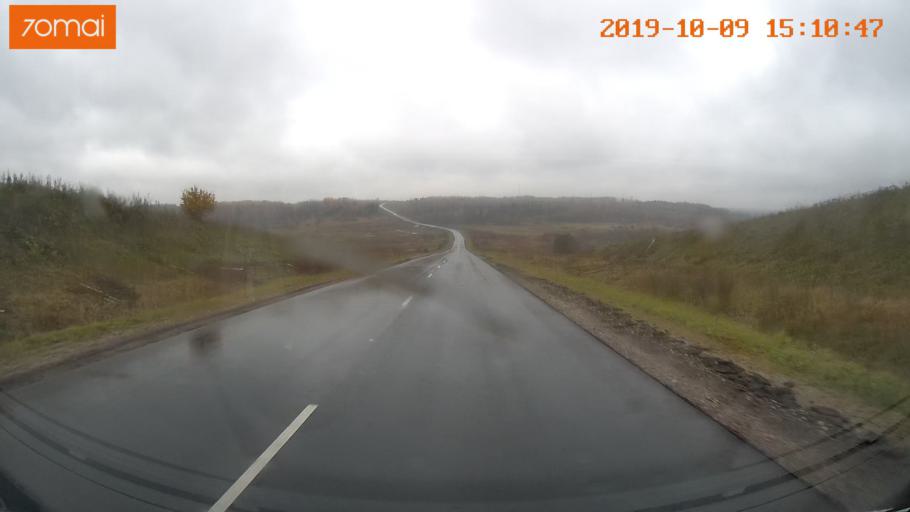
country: RU
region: Kostroma
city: Susanino
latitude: 58.1739
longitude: 41.6365
